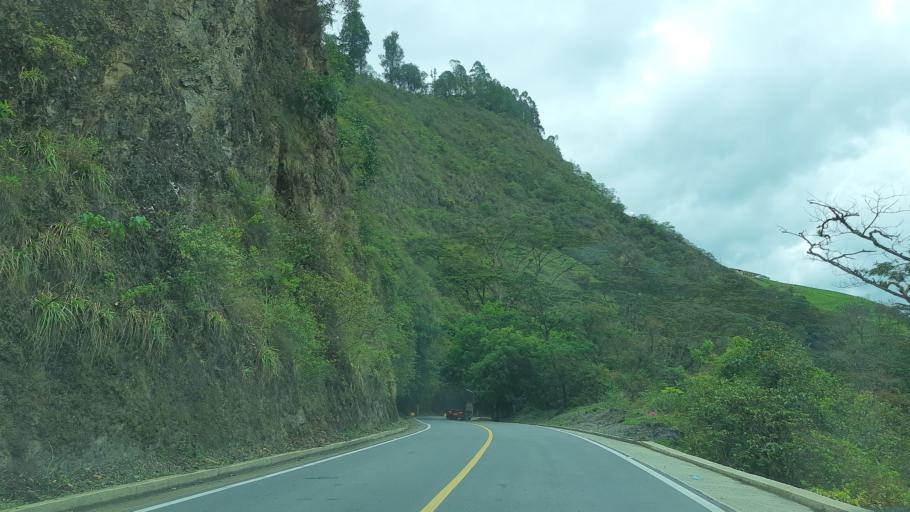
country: CO
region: Boyaca
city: Somondoco
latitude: 4.9806
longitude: -73.3423
